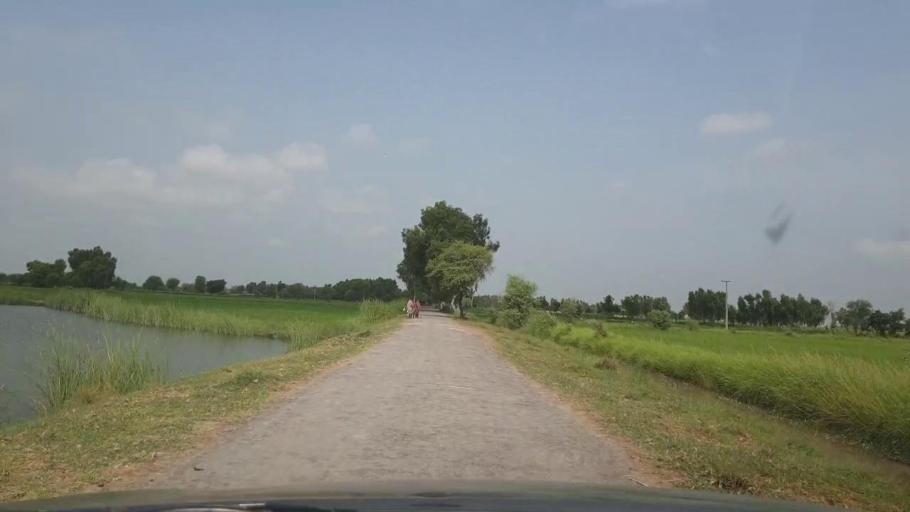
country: PK
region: Sindh
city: Ratodero
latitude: 27.8564
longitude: 68.2985
